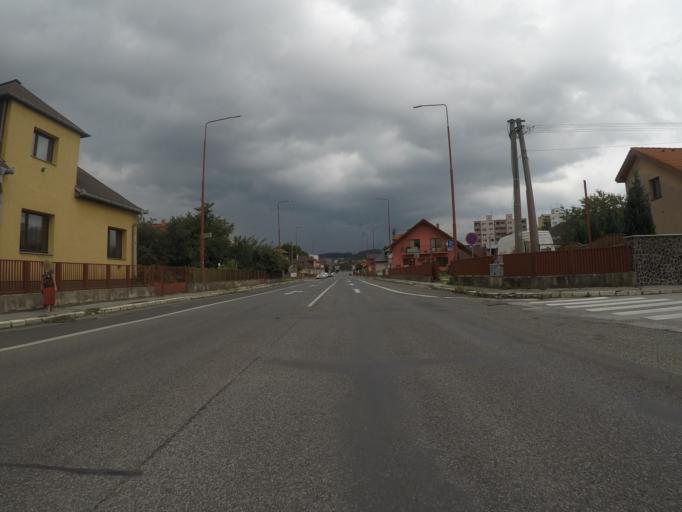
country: SK
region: Kosicky
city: Spisska Nova Ves
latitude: 48.9392
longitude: 20.5589
